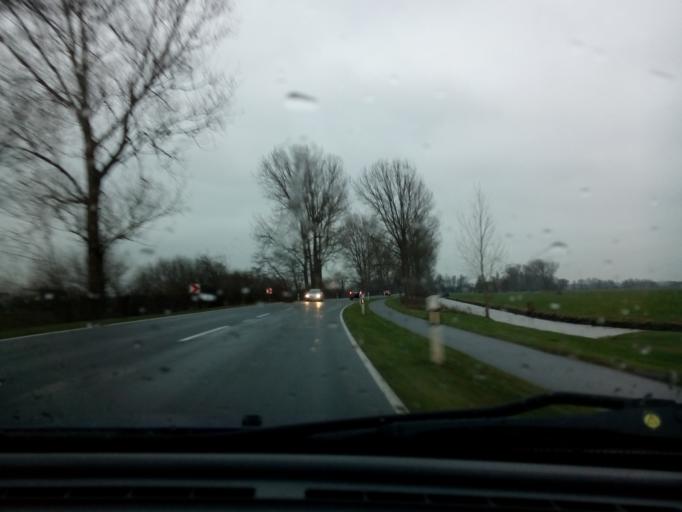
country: DE
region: Lower Saxony
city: Osterholz-Scharmbeck
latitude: 53.2099
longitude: 8.8195
